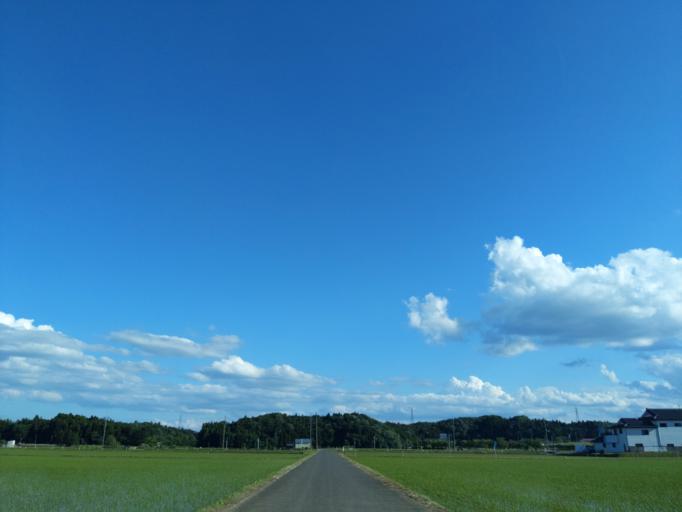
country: JP
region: Fukushima
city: Sukagawa
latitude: 37.3323
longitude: 140.2977
